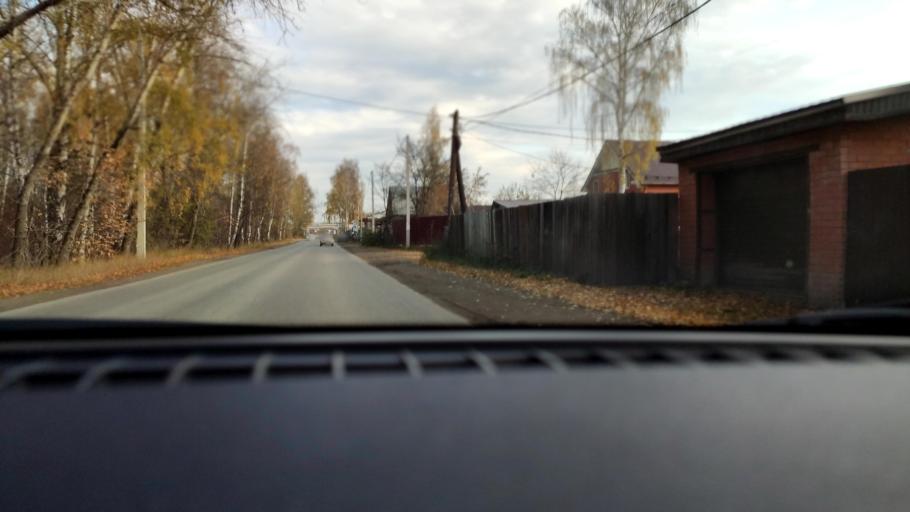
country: RU
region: Perm
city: Kondratovo
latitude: 58.0411
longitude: 56.0257
